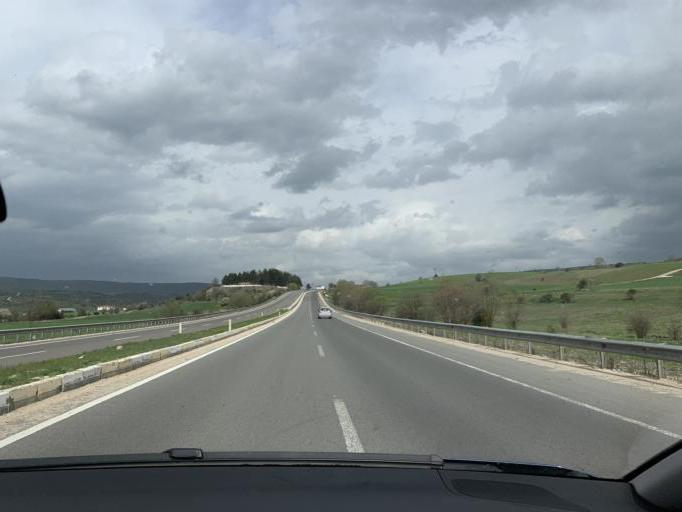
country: TR
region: Bolu
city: Yenicaga
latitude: 40.7815
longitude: 32.0717
